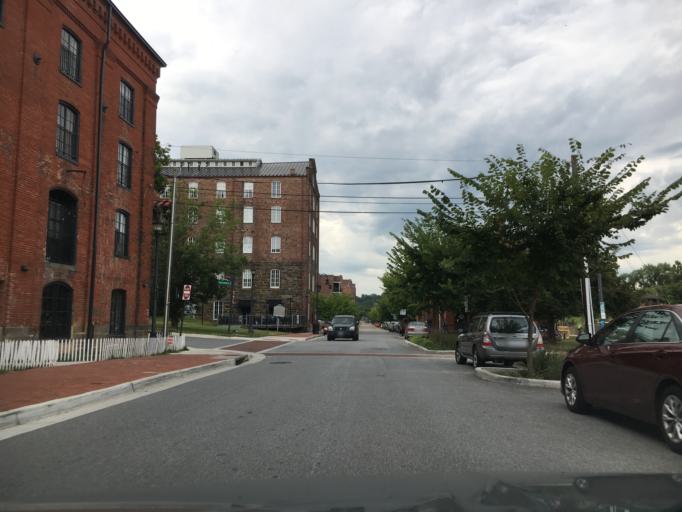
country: US
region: Virginia
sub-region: City of Lynchburg
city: Lynchburg
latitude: 37.4114
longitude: -79.1364
